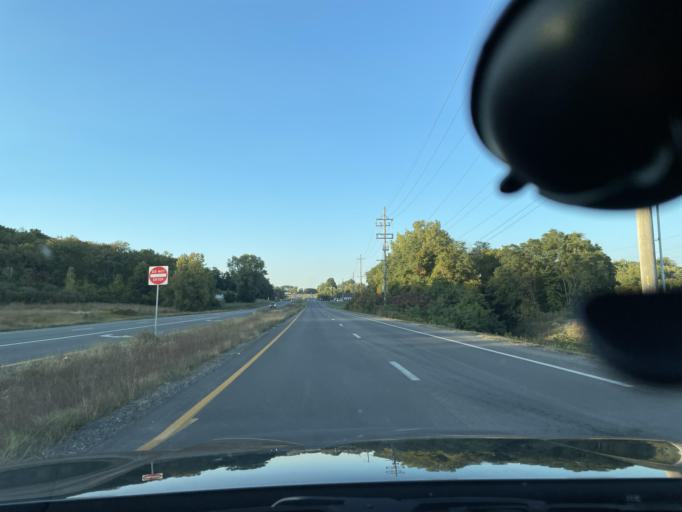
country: US
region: Missouri
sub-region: Andrew County
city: Country Club Village
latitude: 39.8066
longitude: -94.8409
